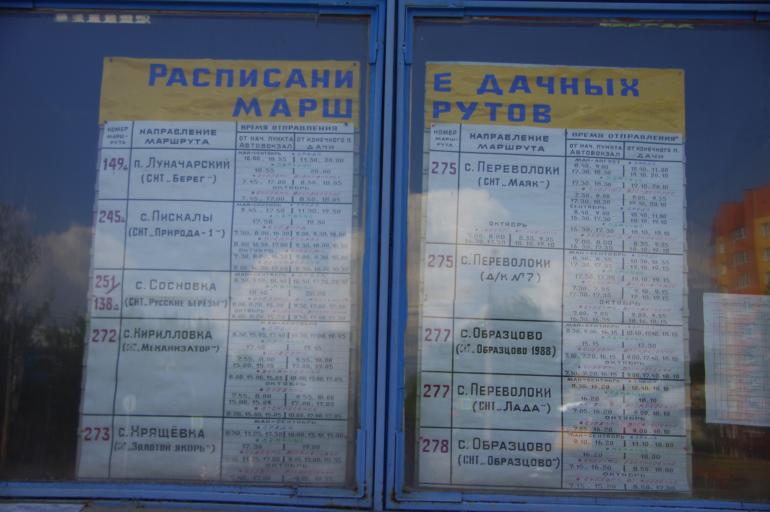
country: RU
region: Samara
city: Tol'yatti
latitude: 53.5013
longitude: 49.3892
